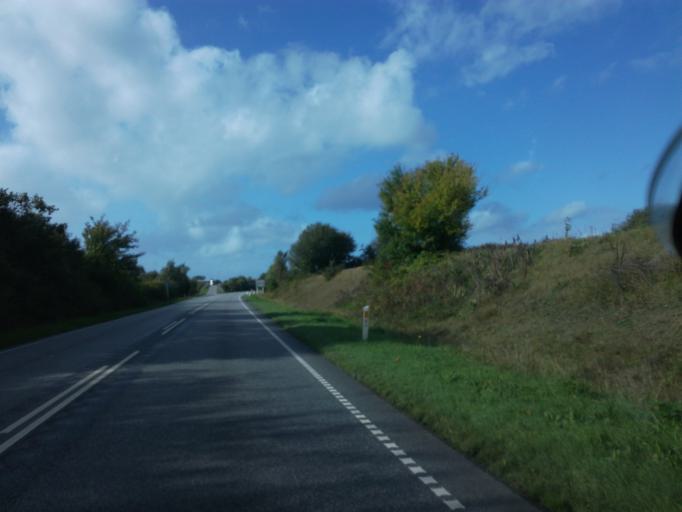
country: DK
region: South Denmark
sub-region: Vejle Kommune
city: Brejning
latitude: 55.6313
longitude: 9.6931
